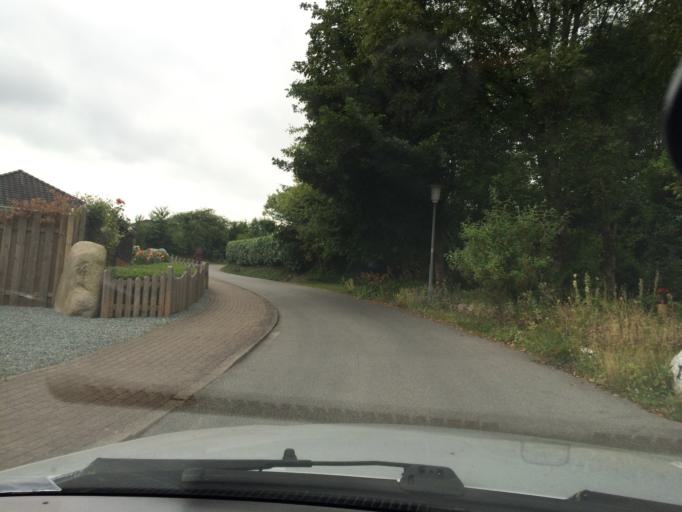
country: DE
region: Schleswig-Holstein
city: Oeversee
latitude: 54.6941
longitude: 9.4280
